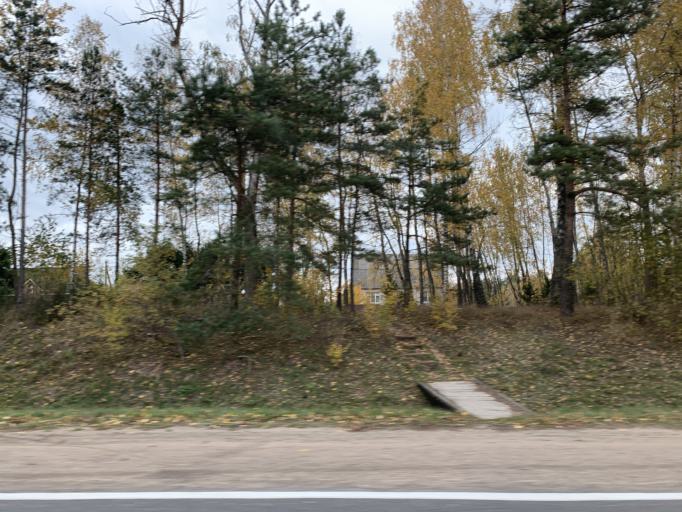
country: BY
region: Minsk
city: Stowbtsy
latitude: 53.4990
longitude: 26.7479
